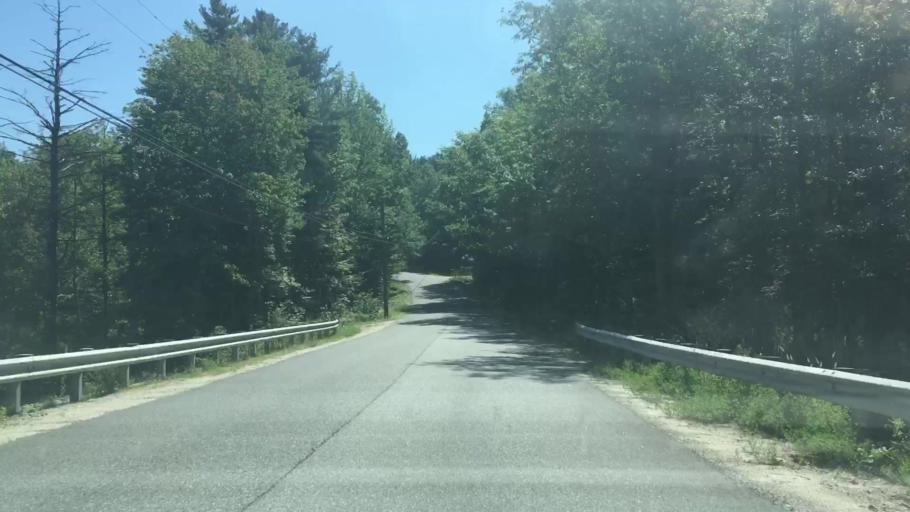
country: US
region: Maine
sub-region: Androscoggin County
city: Sabattus
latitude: 44.1203
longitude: -70.0328
